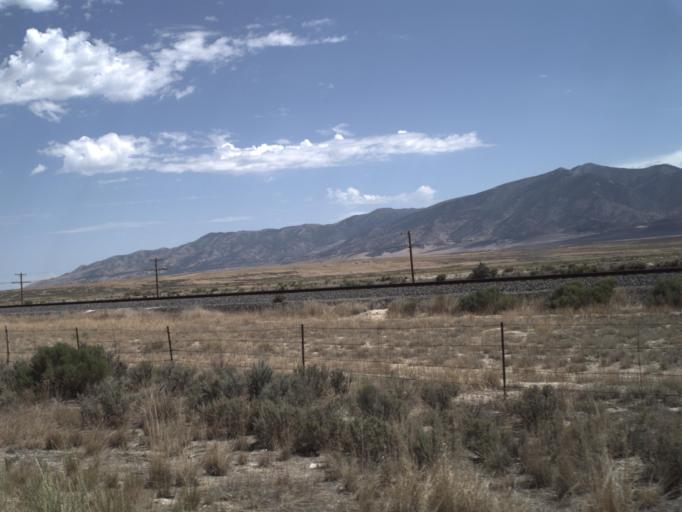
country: US
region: Utah
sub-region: Tooele County
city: Tooele
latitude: 40.3131
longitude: -112.4049
